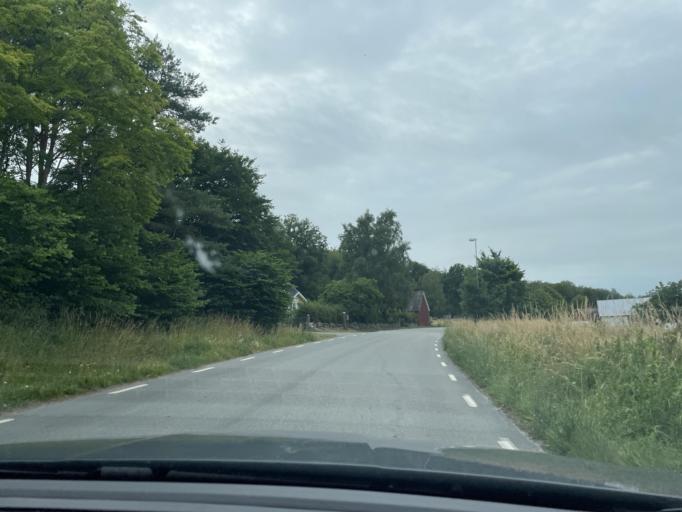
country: SE
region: Blekinge
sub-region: Solvesborgs Kommun
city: Soelvesborg
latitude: 56.0266
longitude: 14.6365
